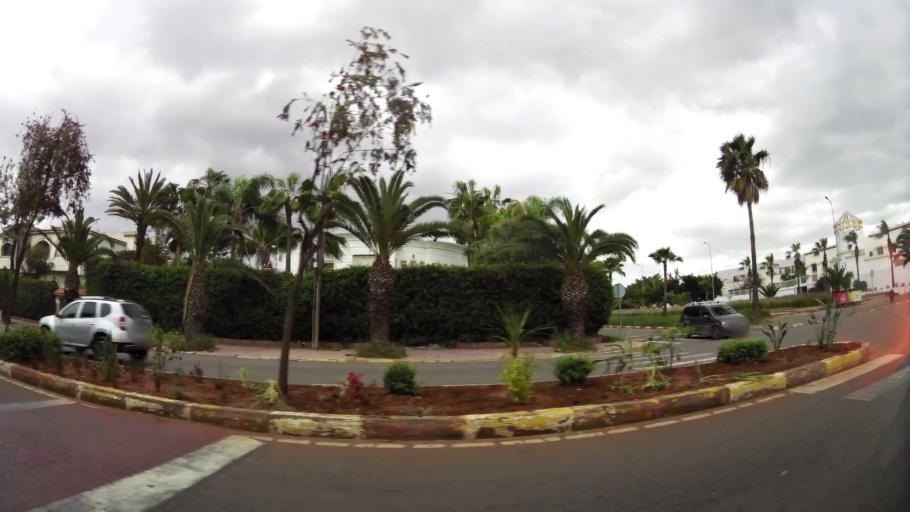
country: MA
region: Grand Casablanca
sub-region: Casablanca
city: Casablanca
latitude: 33.5376
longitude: -7.6308
